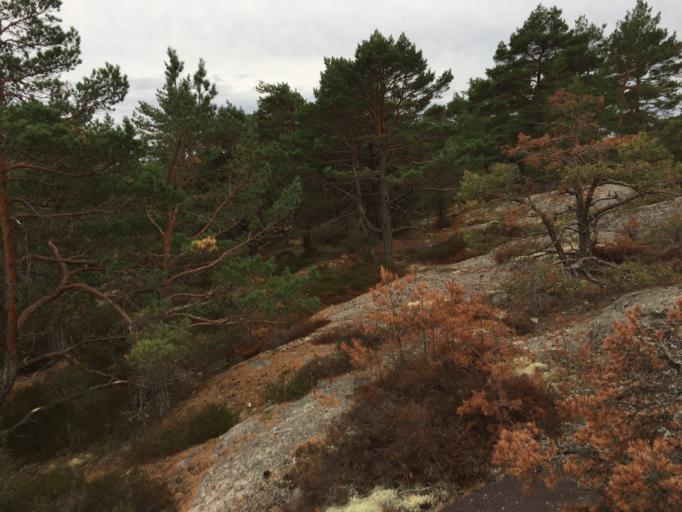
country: NO
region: Ostfold
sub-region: Hvaler
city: Skjaerhalden
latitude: 59.0573
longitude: 11.0348
